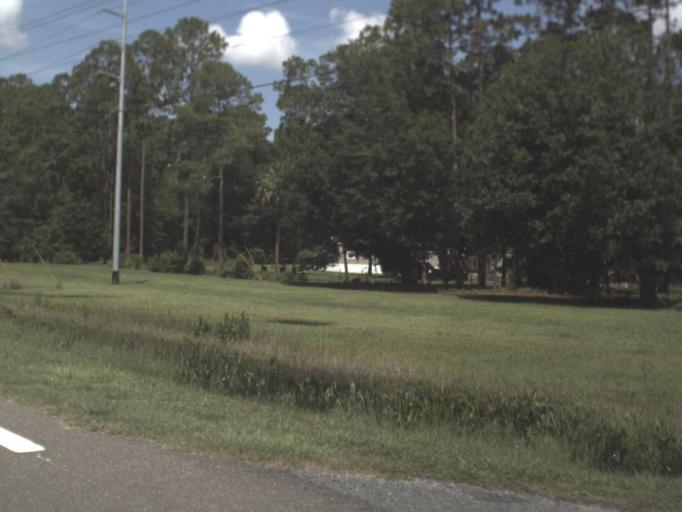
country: US
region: Florida
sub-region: Levy County
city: Chiefland
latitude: 29.3121
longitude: -82.7965
